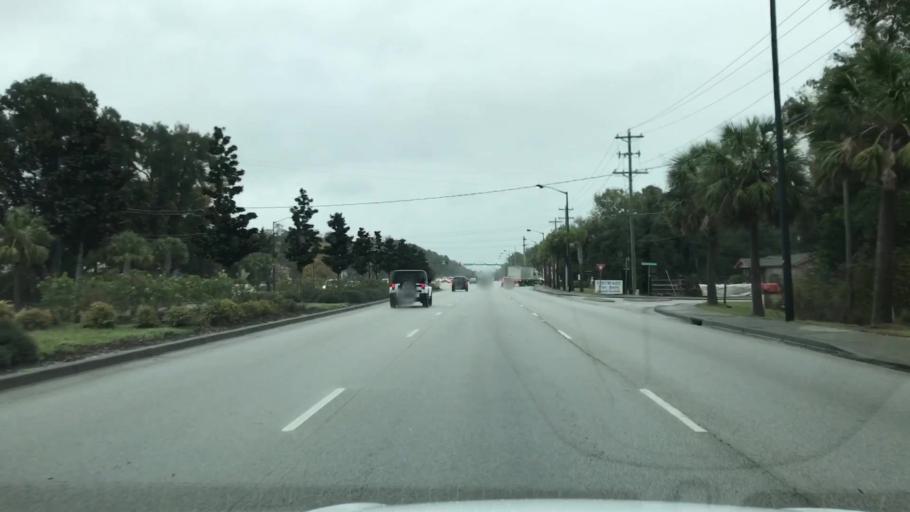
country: US
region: South Carolina
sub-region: Charleston County
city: Isle of Palms
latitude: 32.8602
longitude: -79.7933
